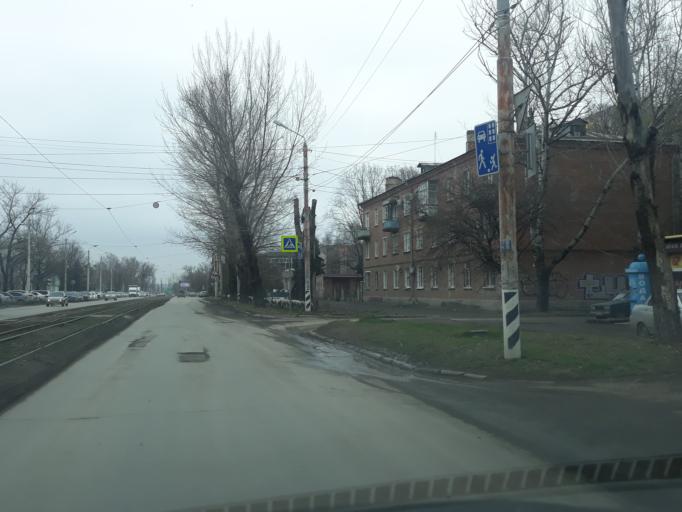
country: RU
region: Rostov
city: Taganrog
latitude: 47.2412
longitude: 38.8895
